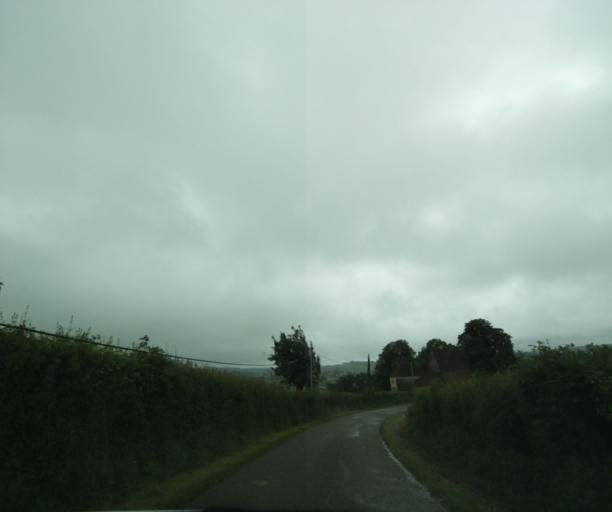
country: FR
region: Bourgogne
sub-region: Departement de Saone-et-Loire
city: Charolles
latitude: 46.3534
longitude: 4.2295
